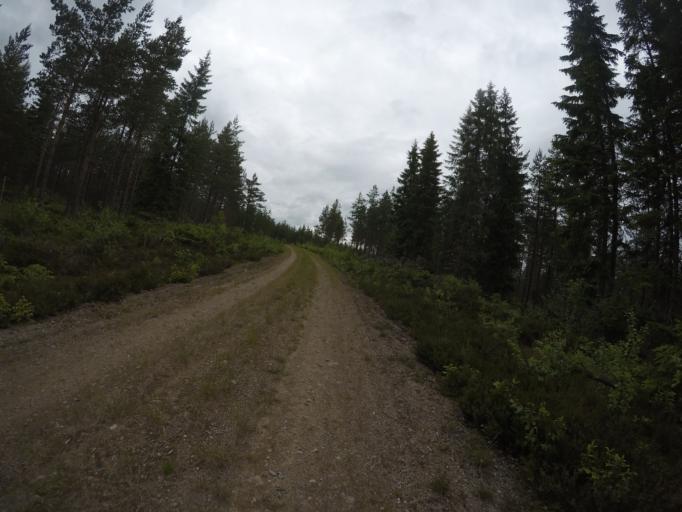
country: SE
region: Dalarna
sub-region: Ludvika Kommun
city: Abborrberget
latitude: 60.0890
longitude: 14.5063
